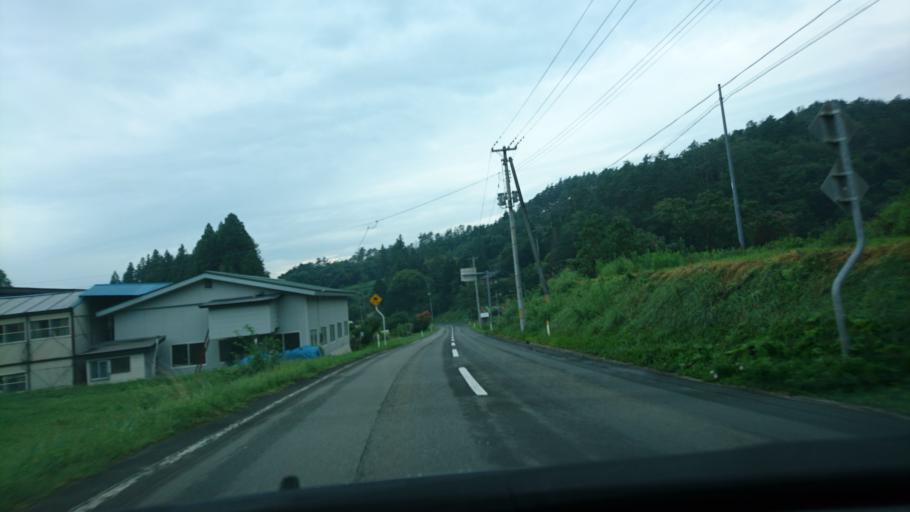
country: JP
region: Iwate
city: Ichinoseki
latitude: 39.0161
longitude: 141.2524
